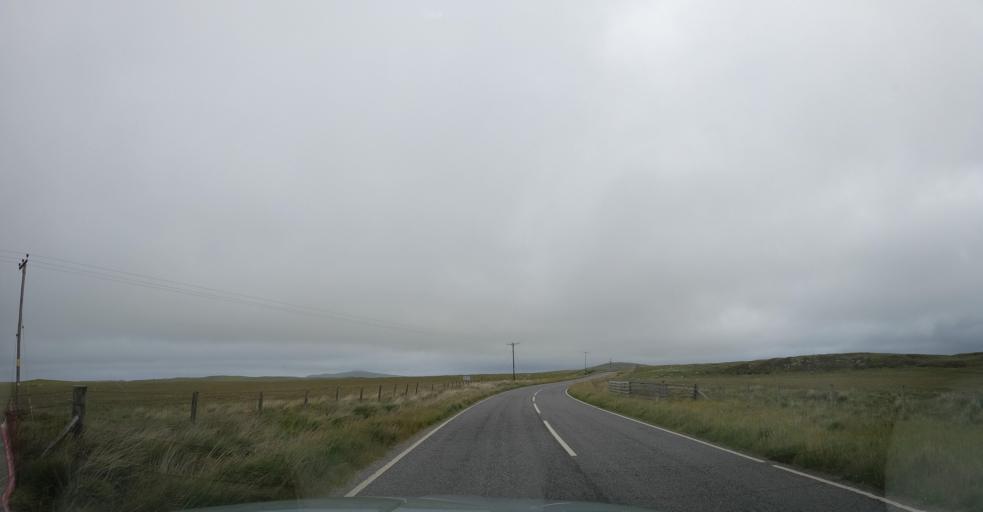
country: GB
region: Scotland
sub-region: Eilean Siar
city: Isle of North Uist
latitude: 57.6942
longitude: -7.1969
